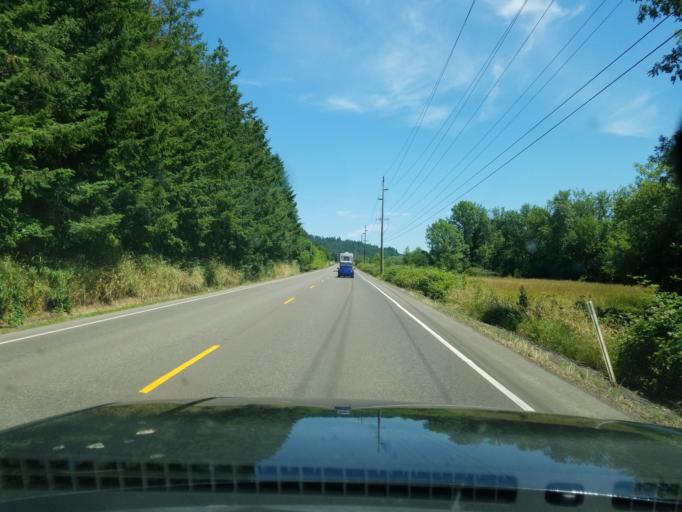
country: US
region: Oregon
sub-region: Yamhill County
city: Yamhill
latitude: 45.3651
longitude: -123.1658
